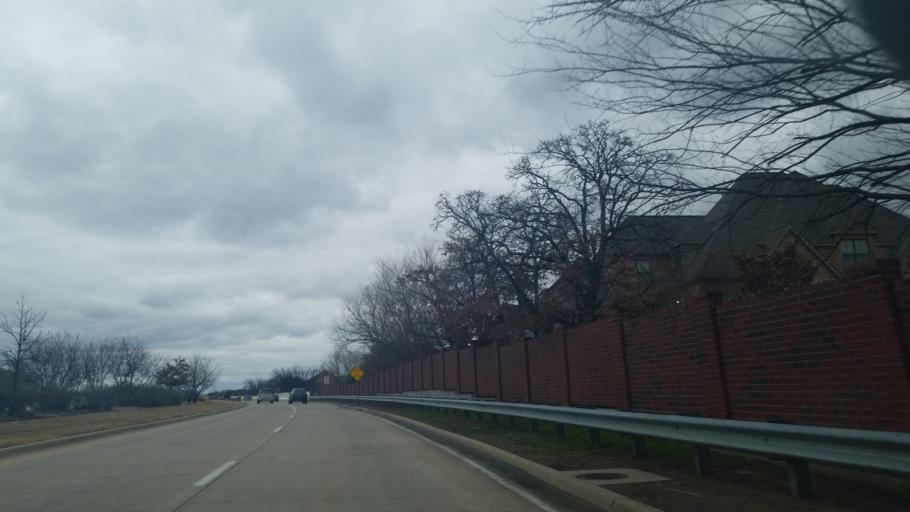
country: US
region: Texas
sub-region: Denton County
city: Copper Canyon
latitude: 33.1011
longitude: -97.0790
